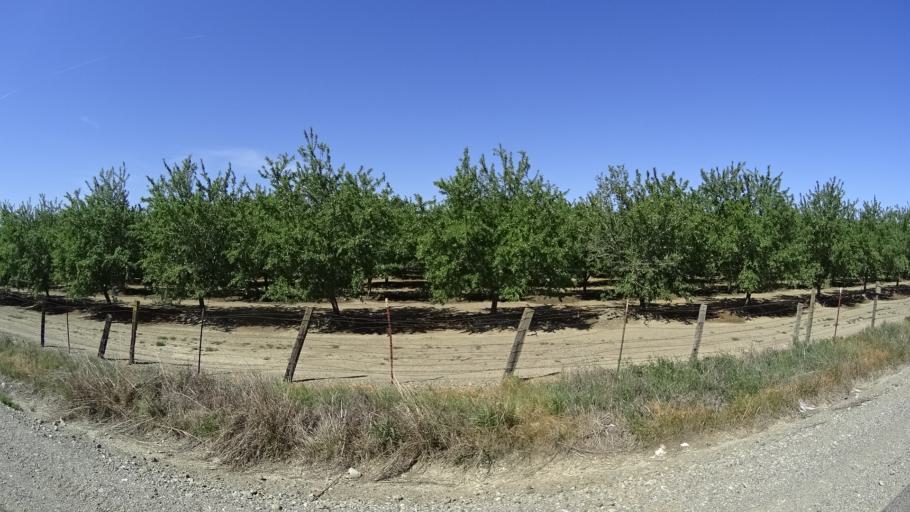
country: US
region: California
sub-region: Glenn County
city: Orland
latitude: 39.7366
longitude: -122.1410
